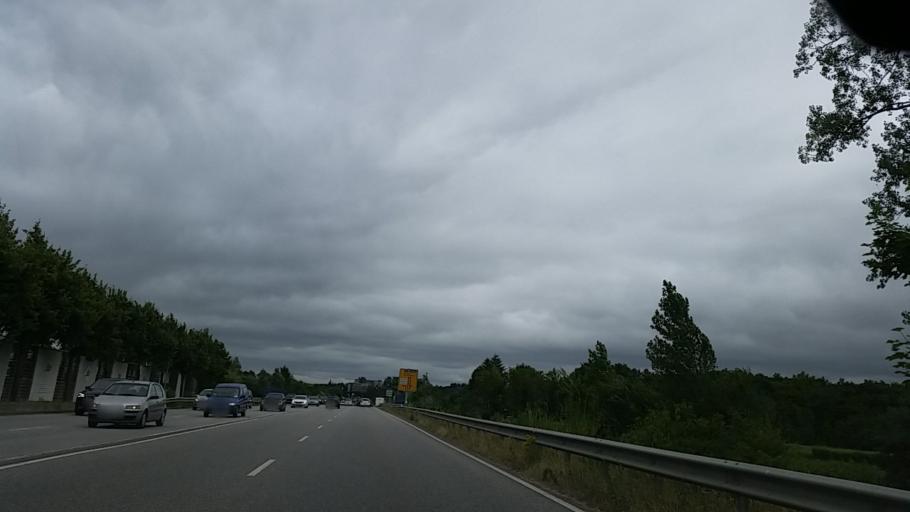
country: DE
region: Schleswig-Holstein
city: Eckernforde
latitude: 54.4714
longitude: 9.8272
